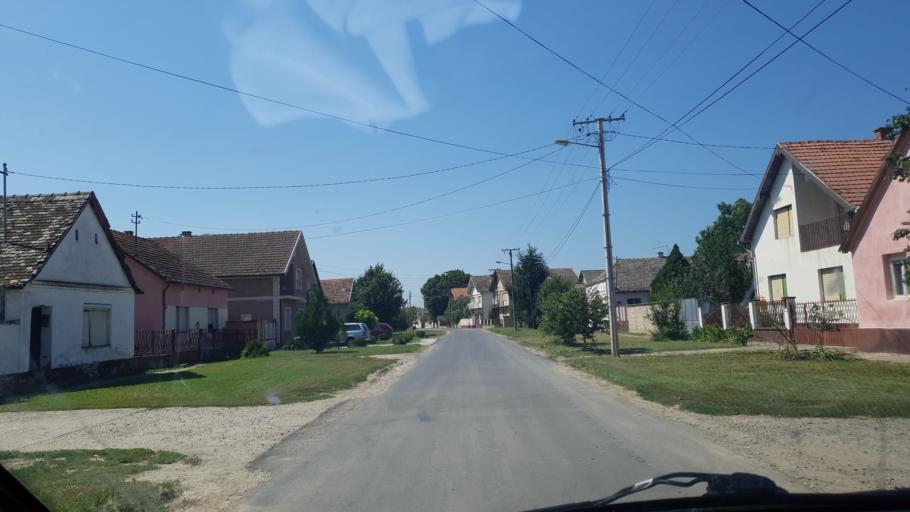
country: RS
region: Autonomna Pokrajina Vojvodina
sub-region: Juznobacki Okrug
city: Kovilj
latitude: 45.2254
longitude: 20.0249
